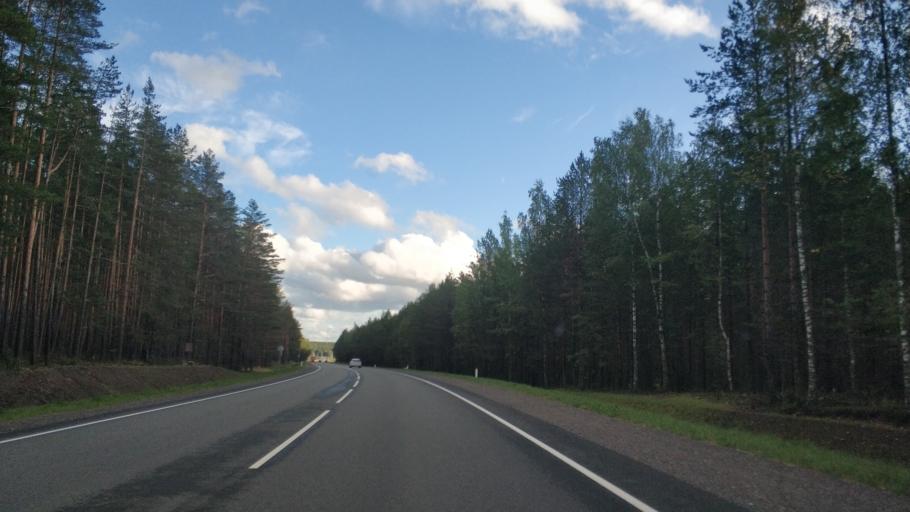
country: RU
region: Leningrad
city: Priozersk
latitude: 60.9852
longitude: 30.1835
